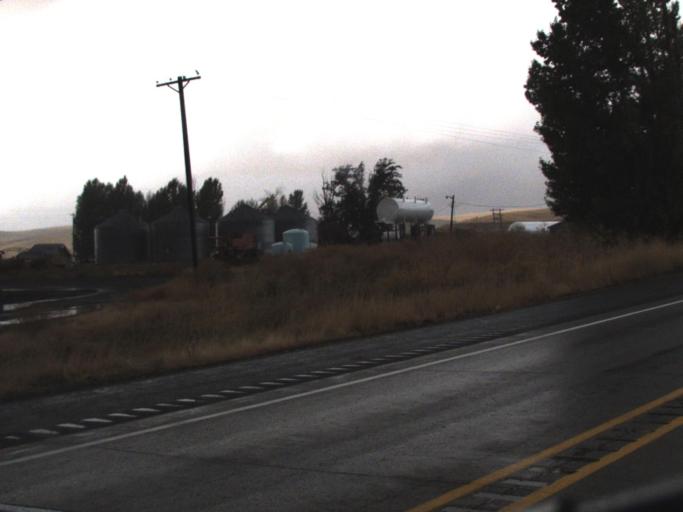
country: US
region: Washington
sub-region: Whitman County
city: Colfax
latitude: 47.0088
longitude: -117.3541
